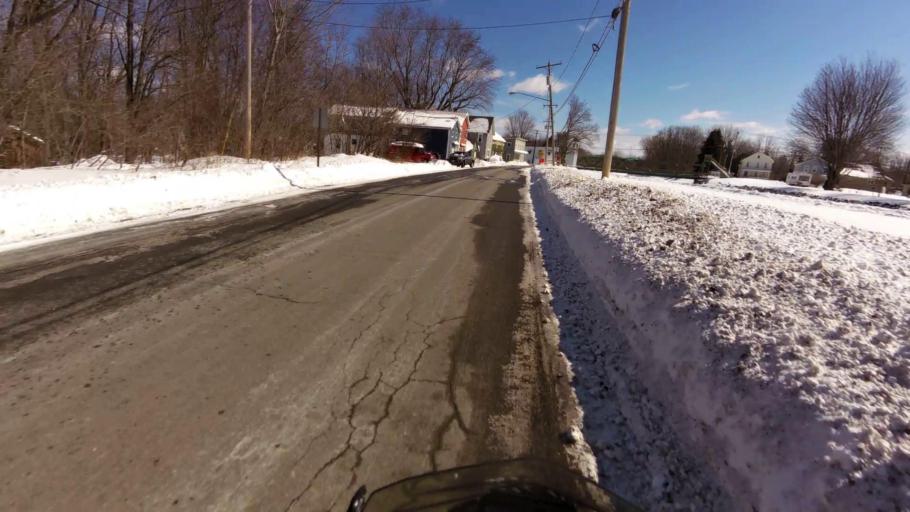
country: US
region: New York
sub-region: Orleans County
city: Holley
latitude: 43.2542
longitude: -78.0679
